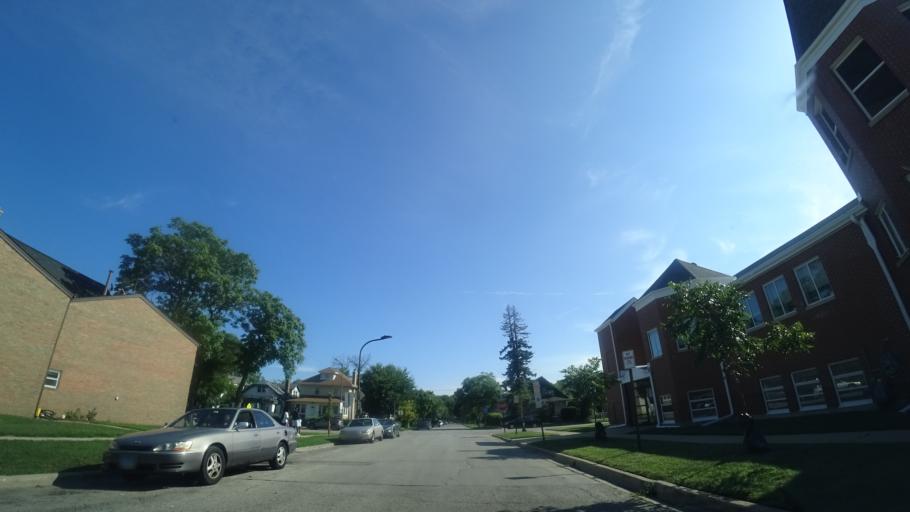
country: US
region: Illinois
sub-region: Cook County
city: Evanston
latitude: 42.0525
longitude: -87.6974
